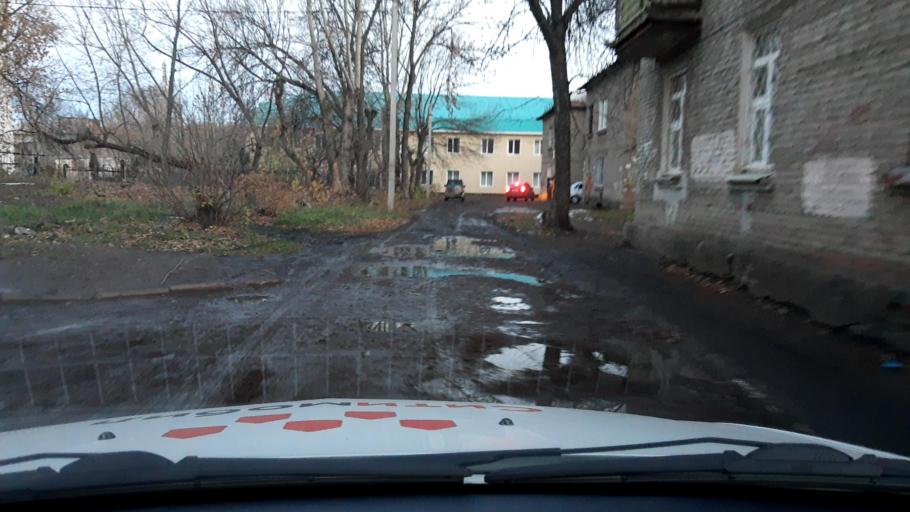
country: RU
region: Bashkortostan
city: Ufa
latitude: 54.8128
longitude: 56.1156
